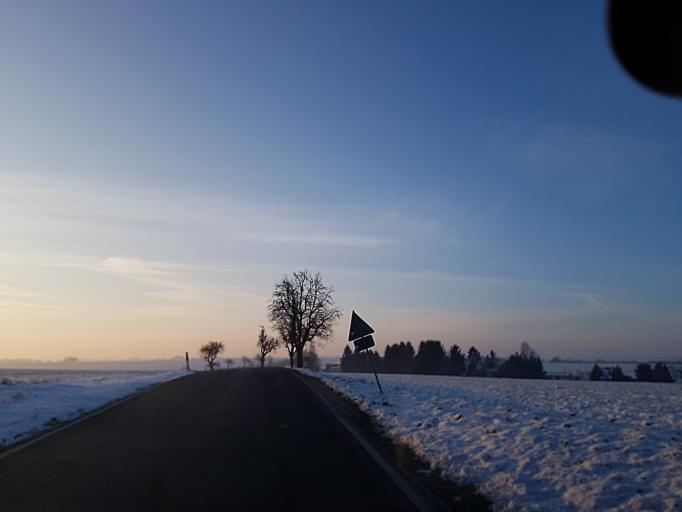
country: DE
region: Saxony
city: Grossweitzschen
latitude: 51.1945
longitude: 13.0307
